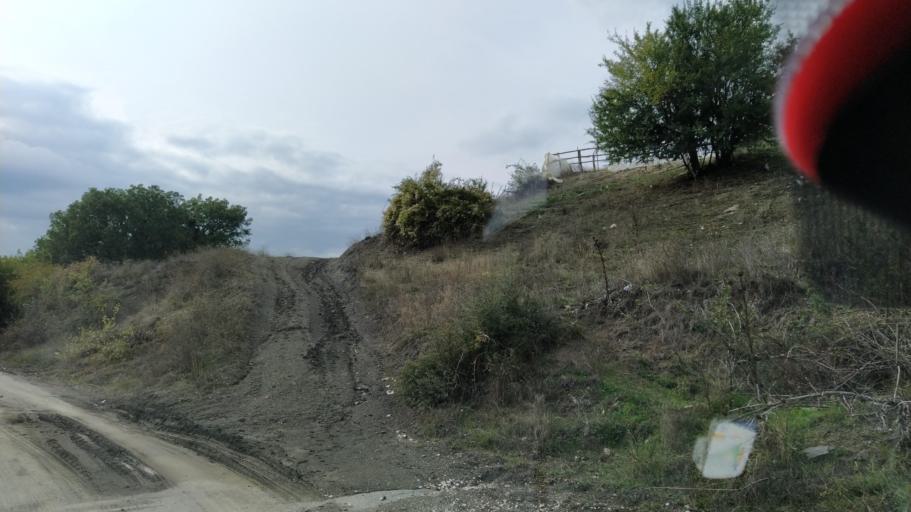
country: MK
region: Strumica
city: Veljusa
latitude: 41.5130
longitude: 22.4912
